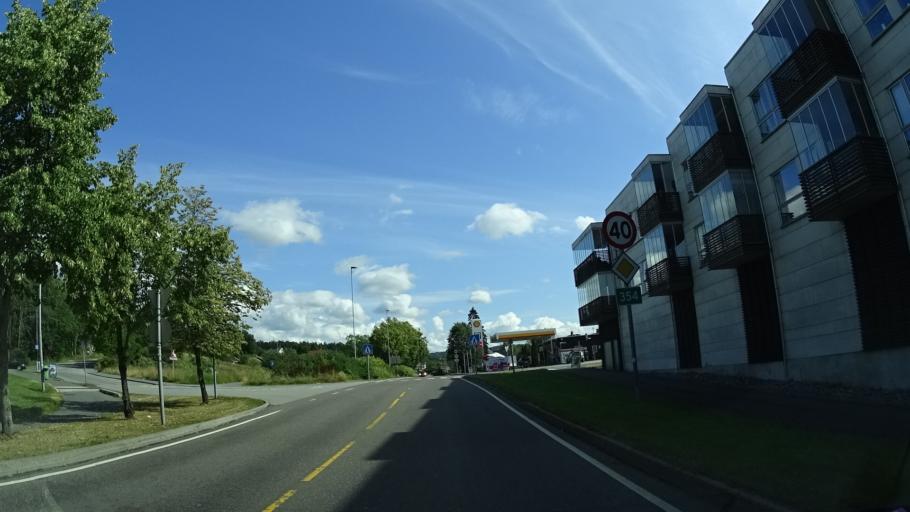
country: NO
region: Telemark
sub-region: Porsgrunn
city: Porsgrunn
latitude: 59.0751
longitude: 9.6832
